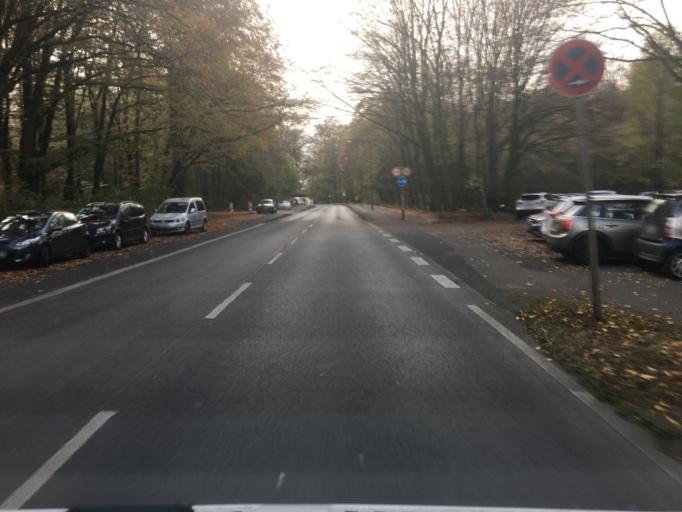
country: DE
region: North Rhine-Westphalia
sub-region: Regierungsbezirk Koln
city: Neustadt/Sued
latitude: 50.9031
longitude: 6.9065
